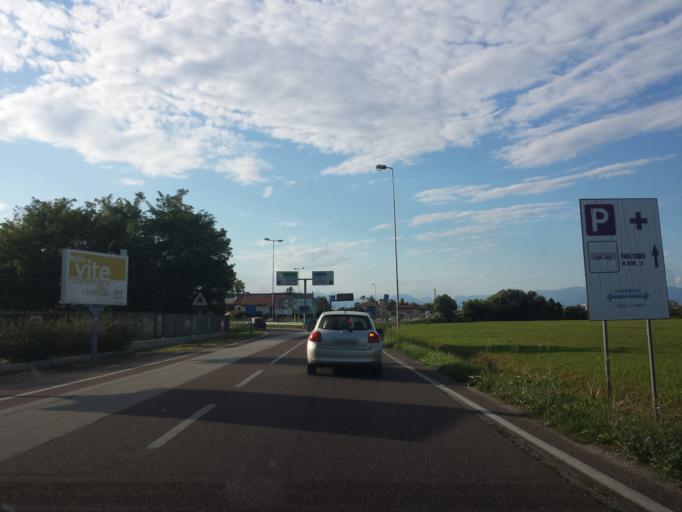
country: IT
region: Veneto
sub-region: Provincia di Vicenza
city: Villaggio Montegrappa
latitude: 45.5328
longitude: 11.5913
